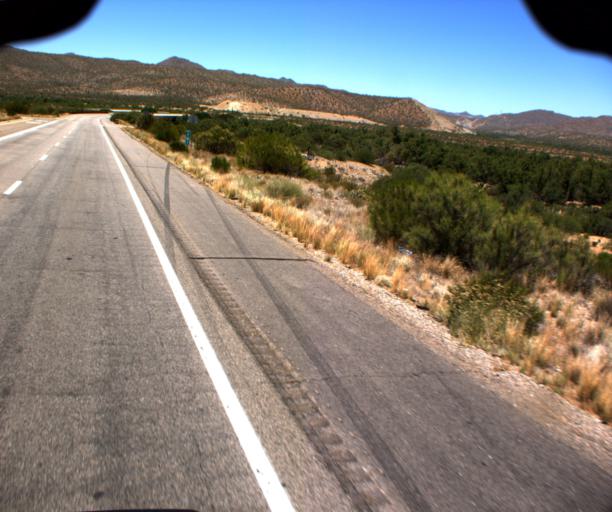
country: US
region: Arizona
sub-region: Yavapai County
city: Bagdad
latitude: 34.3679
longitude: -113.1805
